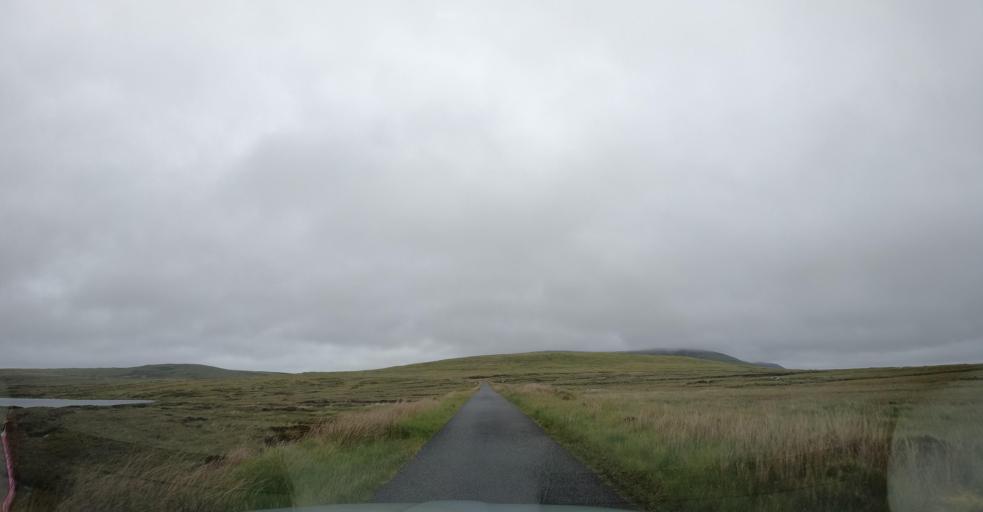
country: GB
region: Scotland
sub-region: Eilean Siar
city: Isle of North Uist
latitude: 57.5922
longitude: -7.3887
